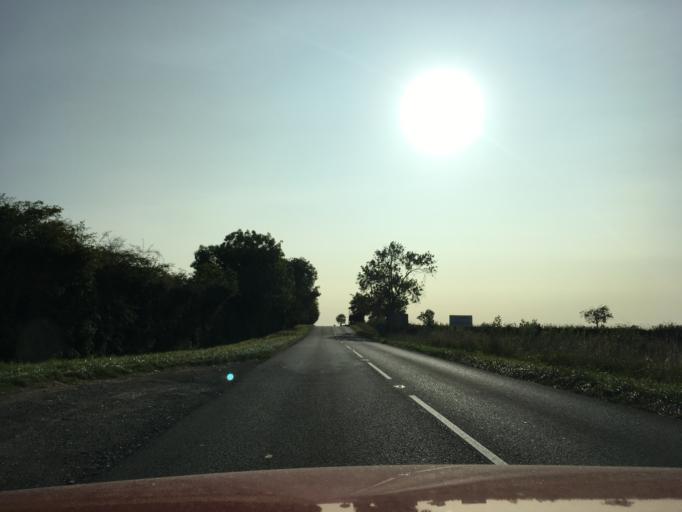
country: GB
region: England
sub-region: Gloucestershire
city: Gloucester
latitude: 51.9624
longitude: -2.2742
